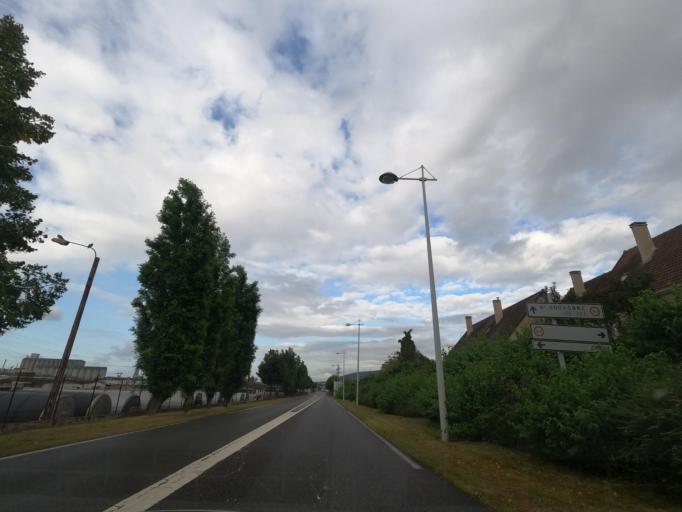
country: FR
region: Haute-Normandie
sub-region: Departement de la Seine-Maritime
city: Grand-Couronne
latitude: 49.3462
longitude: 0.9890
